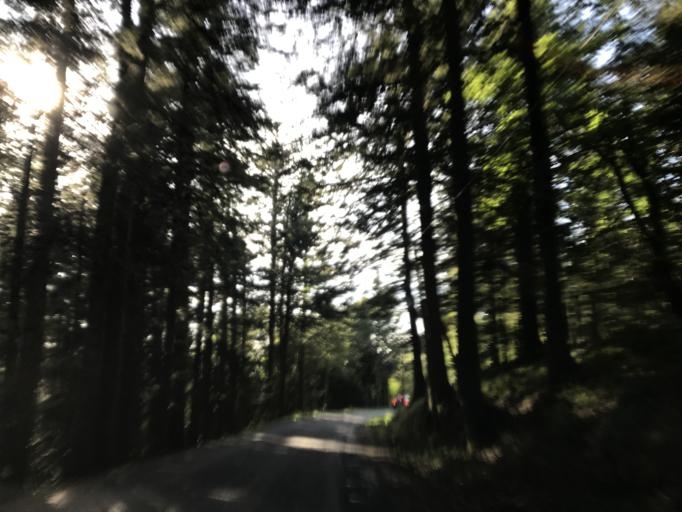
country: FR
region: Auvergne
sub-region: Departement du Puy-de-Dome
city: Job
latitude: 45.6809
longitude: 3.7586
